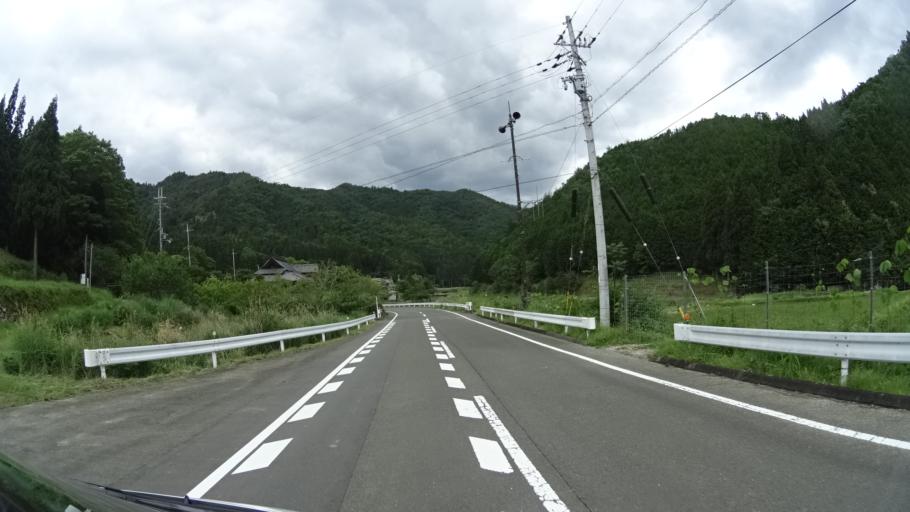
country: JP
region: Hyogo
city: Sasayama
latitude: 35.0552
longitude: 135.3977
